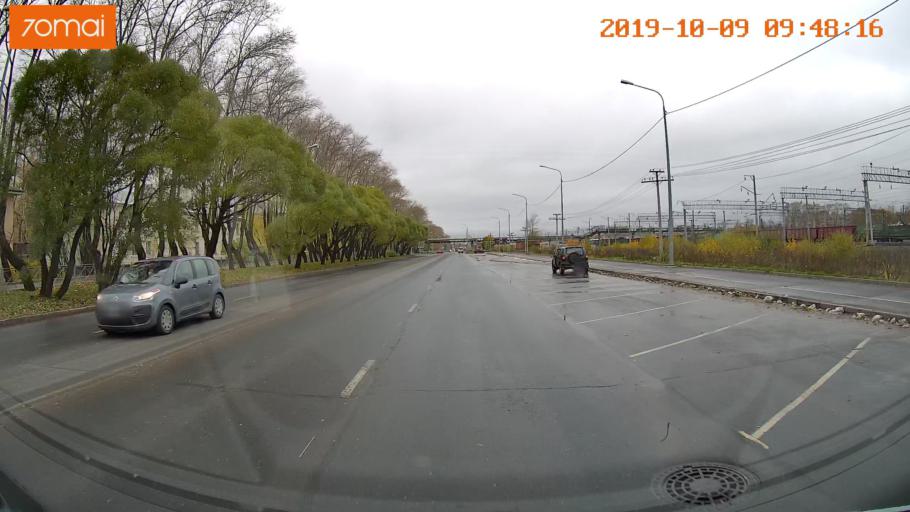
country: RU
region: Vologda
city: Vologda
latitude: 59.1938
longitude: 39.9313
